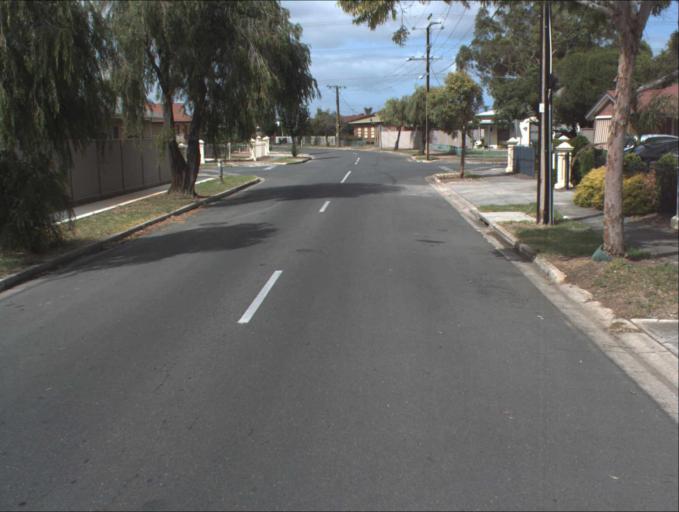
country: AU
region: South Australia
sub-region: Charles Sturt
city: Woodville
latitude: -34.8697
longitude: 138.5600
